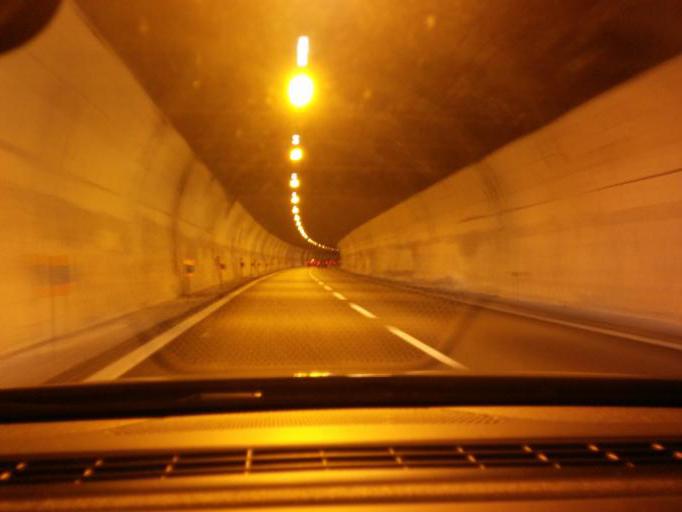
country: IT
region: Liguria
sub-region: Provincia di Savona
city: Celle Ligure
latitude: 44.3385
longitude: 8.5315
